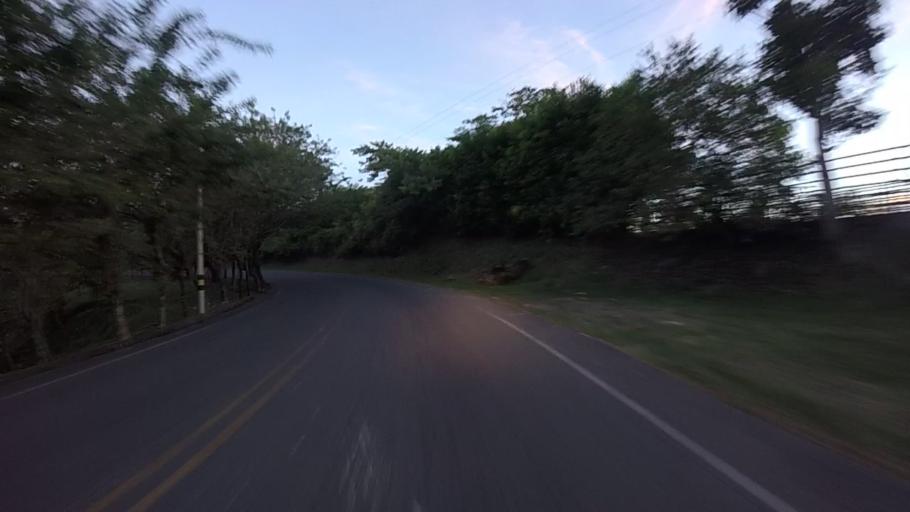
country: CO
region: Valle del Cauca
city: Cartago
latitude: 4.7260
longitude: -75.8902
